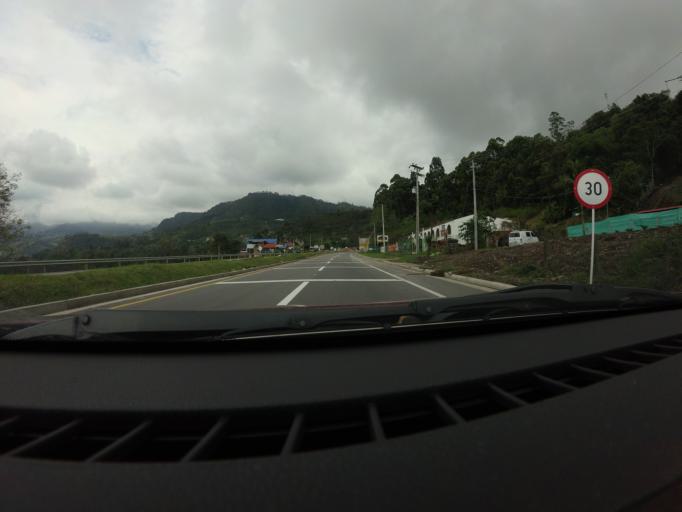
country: CO
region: Cundinamarca
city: San Francisco
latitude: 4.9623
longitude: -74.3029
